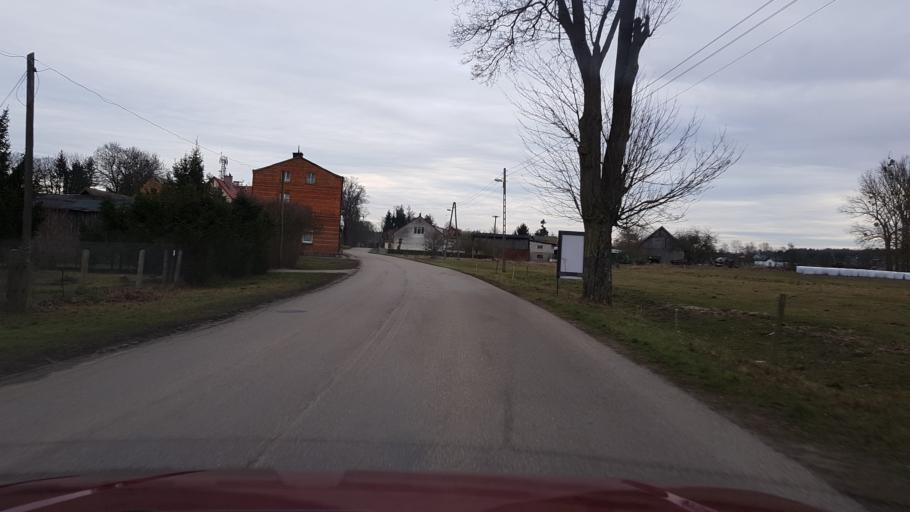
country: PL
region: West Pomeranian Voivodeship
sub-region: Powiat policki
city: Dobra
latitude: 53.5483
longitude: 14.4604
